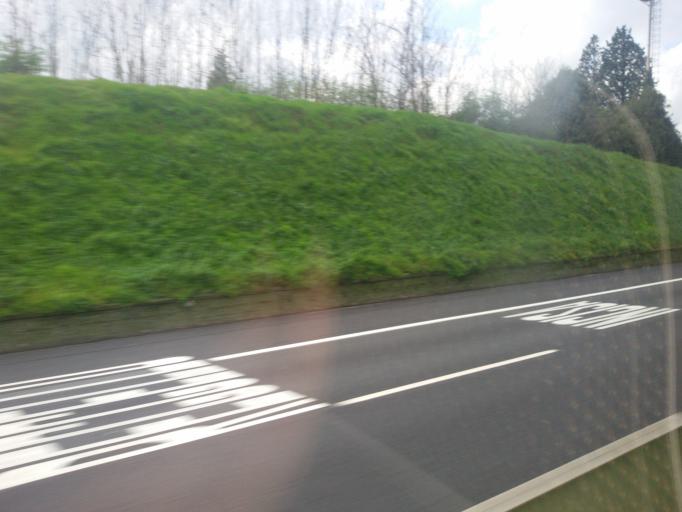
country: IT
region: Tuscany
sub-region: Province of Florence
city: Incisa in Val d'Arno
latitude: 43.6677
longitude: 11.4579
